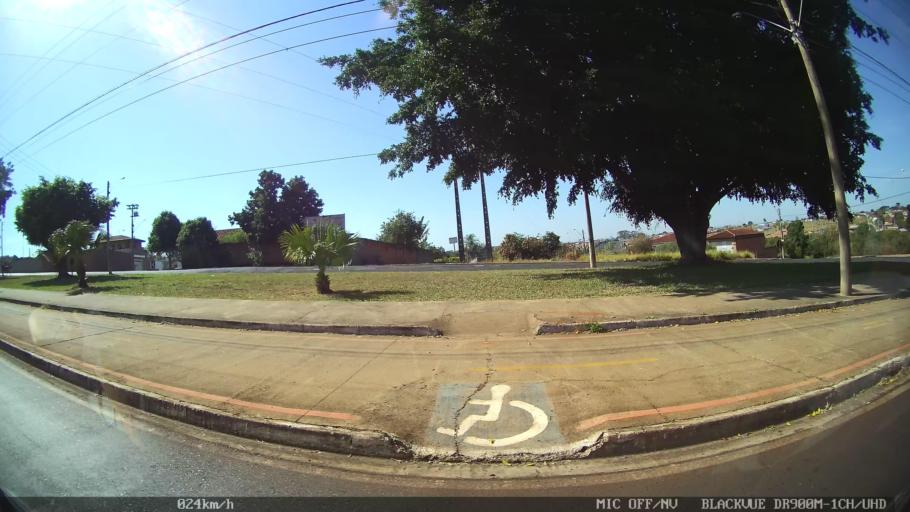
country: BR
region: Sao Paulo
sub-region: Batatais
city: Batatais
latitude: -20.9062
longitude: -47.5822
